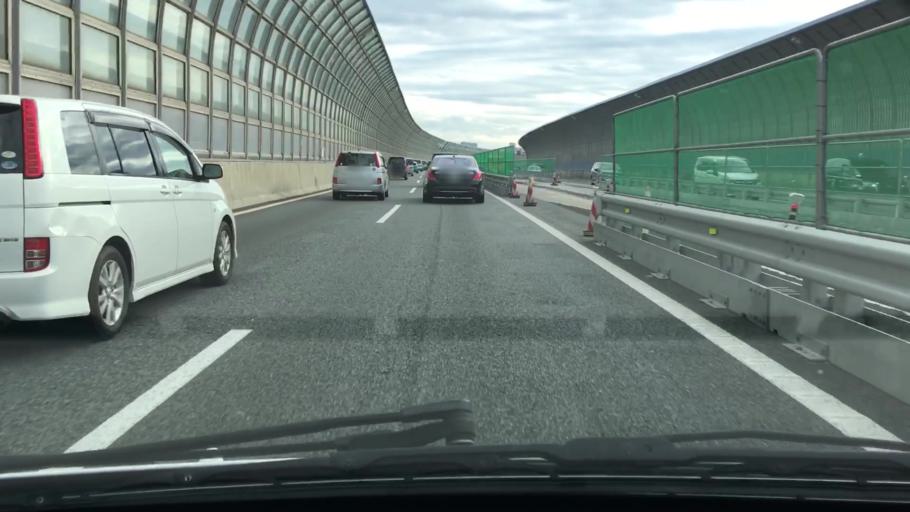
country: JP
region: Chiba
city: Funabashi
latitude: 35.6927
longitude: 139.9826
